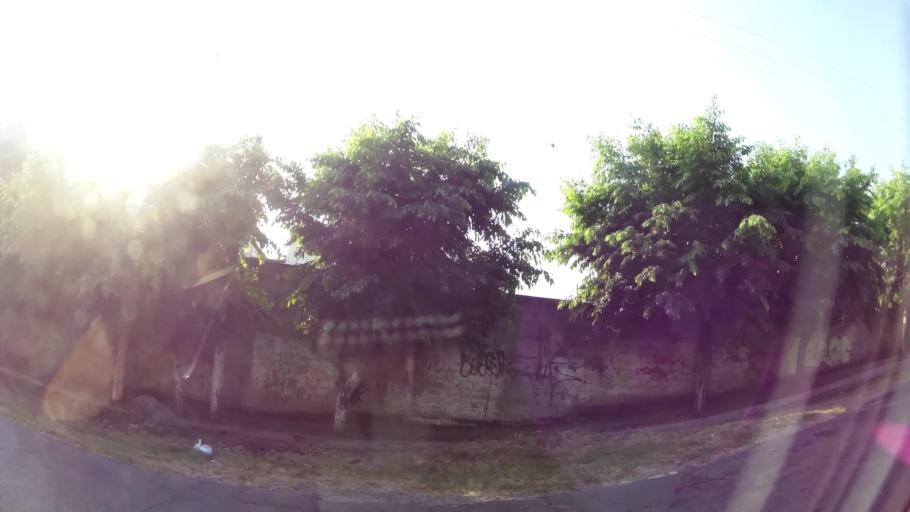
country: SV
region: San Salvador
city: San Salvador
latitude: 13.6842
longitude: -89.2041
